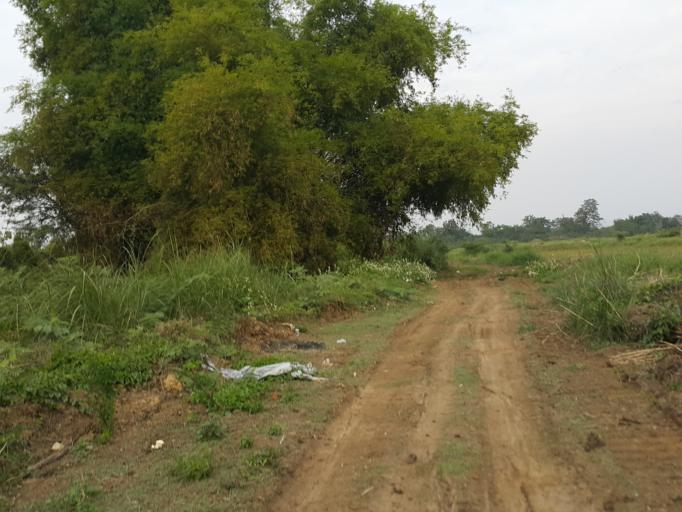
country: TH
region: Chiang Mai
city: San Kamphaeng
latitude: 18.7984
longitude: 99.1158
